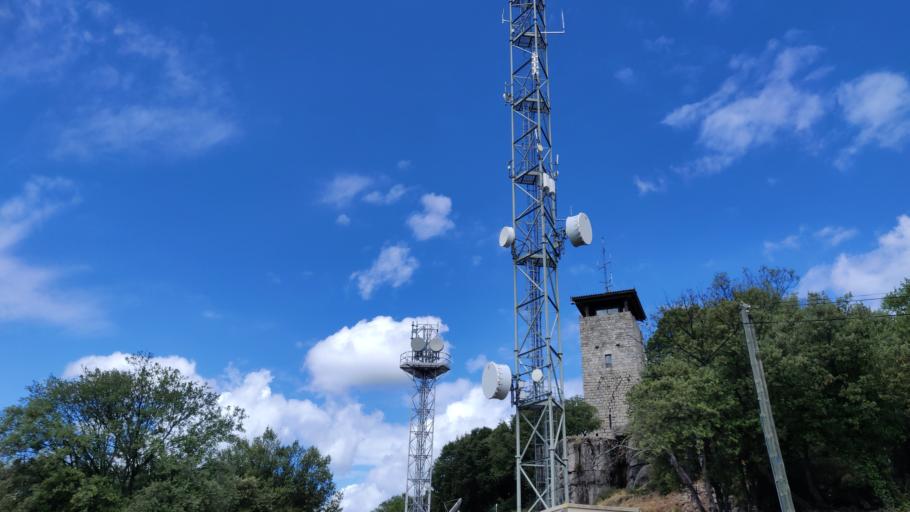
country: FR
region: Rhone-Alpes
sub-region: Departement de l'Ardeche
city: Joyeuse
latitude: 44.5449
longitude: 4.2172
